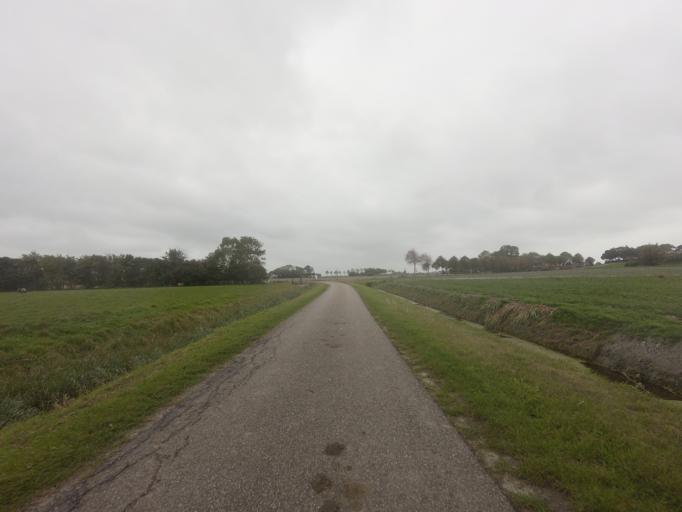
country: NL
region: Friesland
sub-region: Gemeente Ferwerderadiel
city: Ferwert
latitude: 53.3367
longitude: 5.8557
